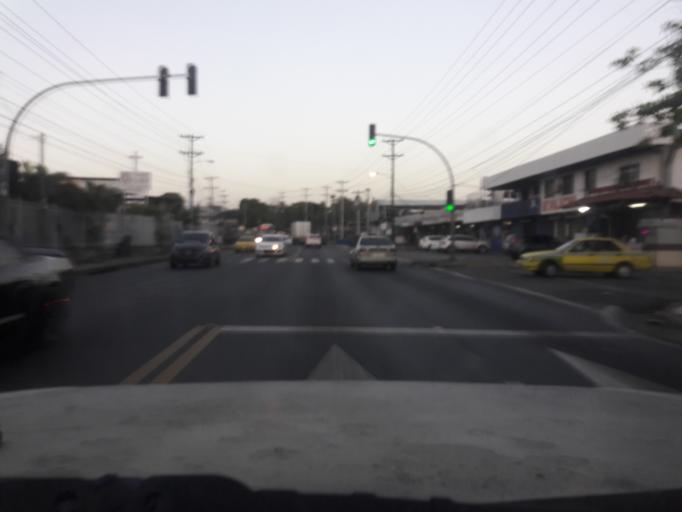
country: PA
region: Panama
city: San Miguelito
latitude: 9.0499
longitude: -79.4376
